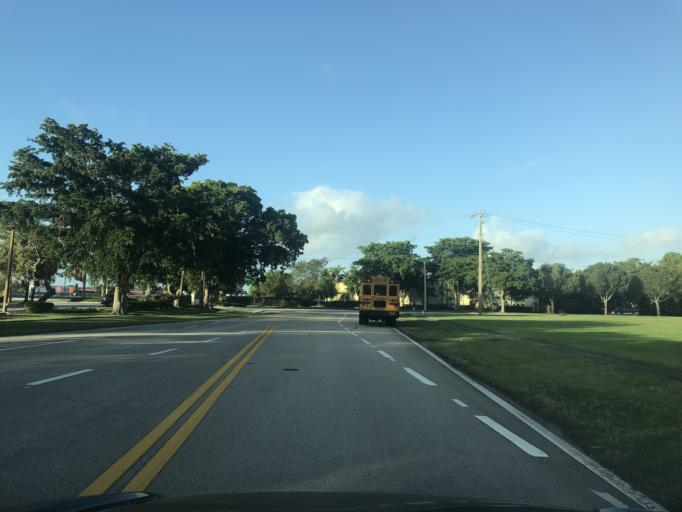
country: US
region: Florida
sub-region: Broward County
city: Pine Island Ridge
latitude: 26.1188
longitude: -80.3236
